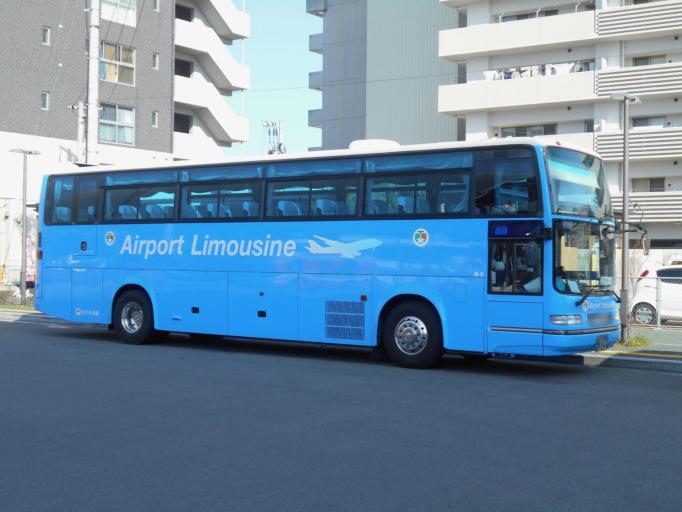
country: JP
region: Kochi
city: Kochi-shi
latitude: 33.5678
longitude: 133.5445
